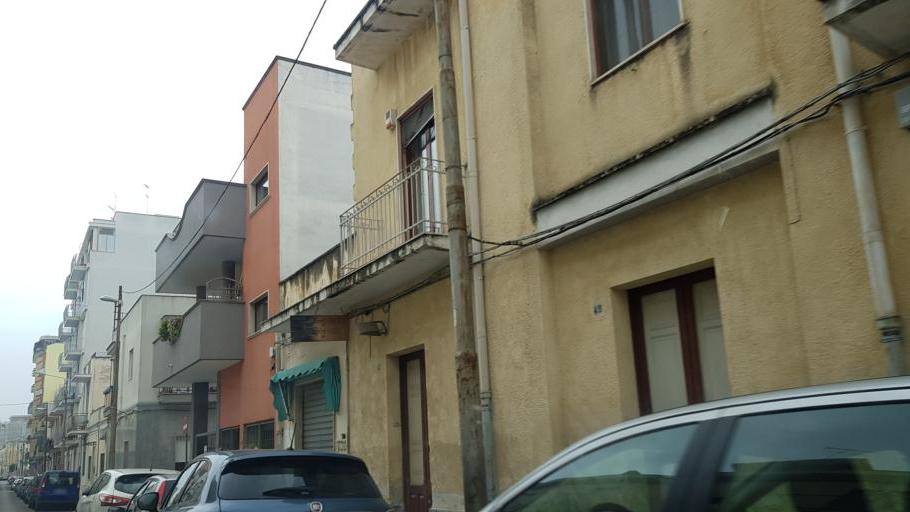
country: IT
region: Apulia
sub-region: Provincia di Brindisi
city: Brindisi
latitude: 40.6315
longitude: 17.9343
